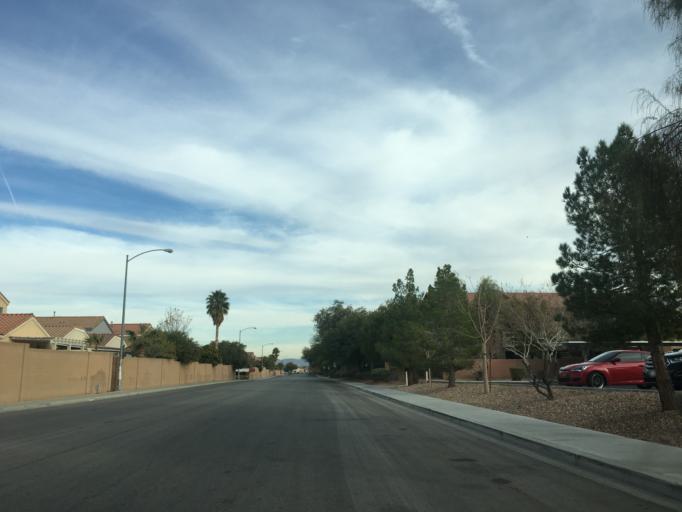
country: US
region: Nevada
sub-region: Clark County
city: Enterprise
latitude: 36.0153
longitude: -115.1783
